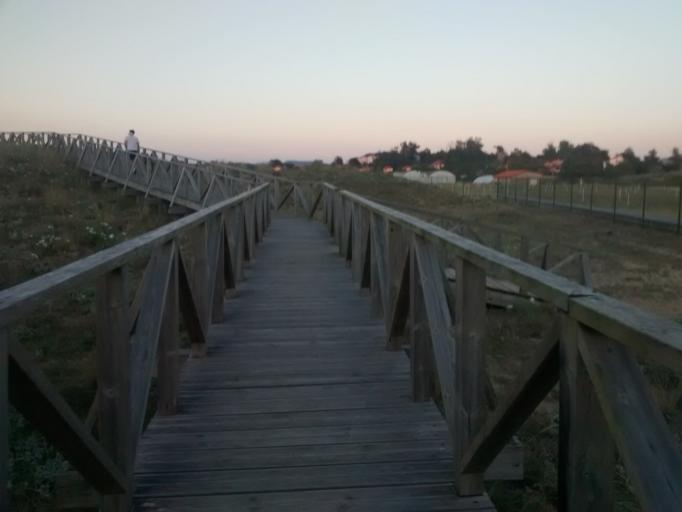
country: ES
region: Cantabria
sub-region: Provincia de Cantabria
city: Santander
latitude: 43.4599
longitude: -3.7293
